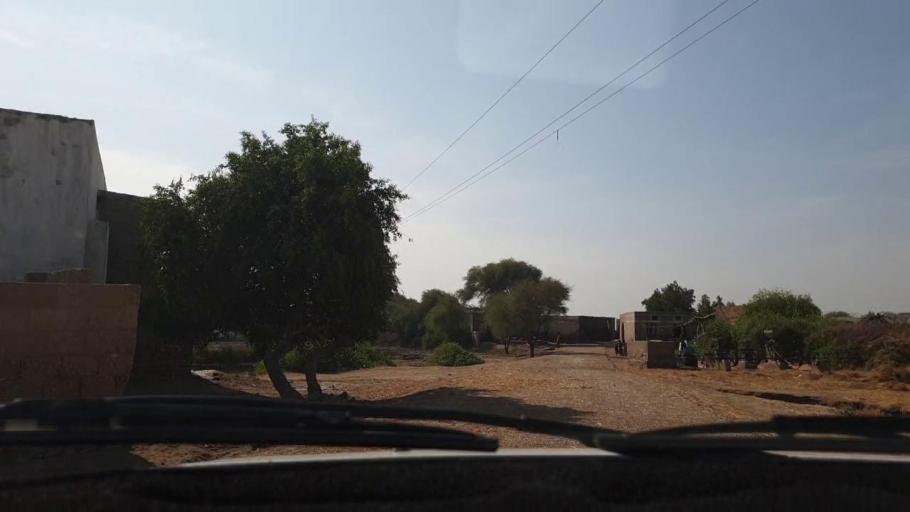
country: PK
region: Sindh
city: Kario
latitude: 24.9012
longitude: 68.4937
